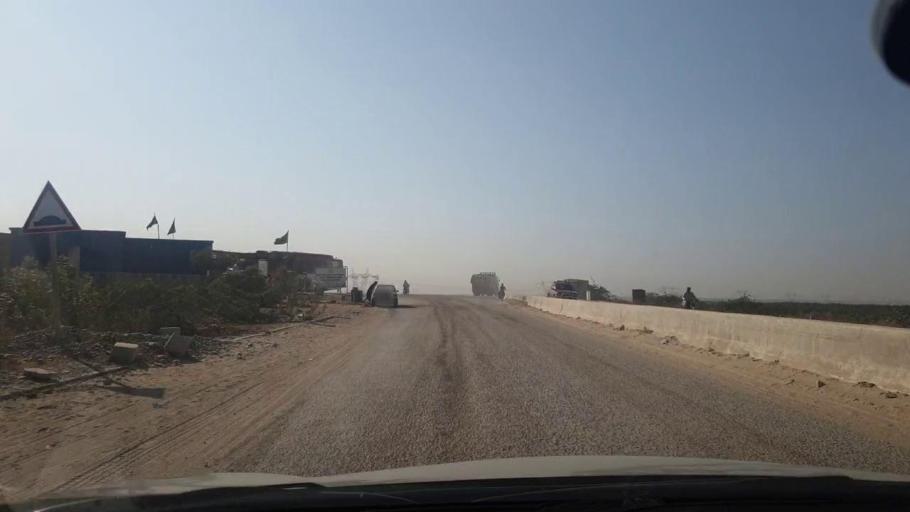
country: PK
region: Sindh
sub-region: Karachi District
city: Karachi
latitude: 25.0754
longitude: 67.0139
